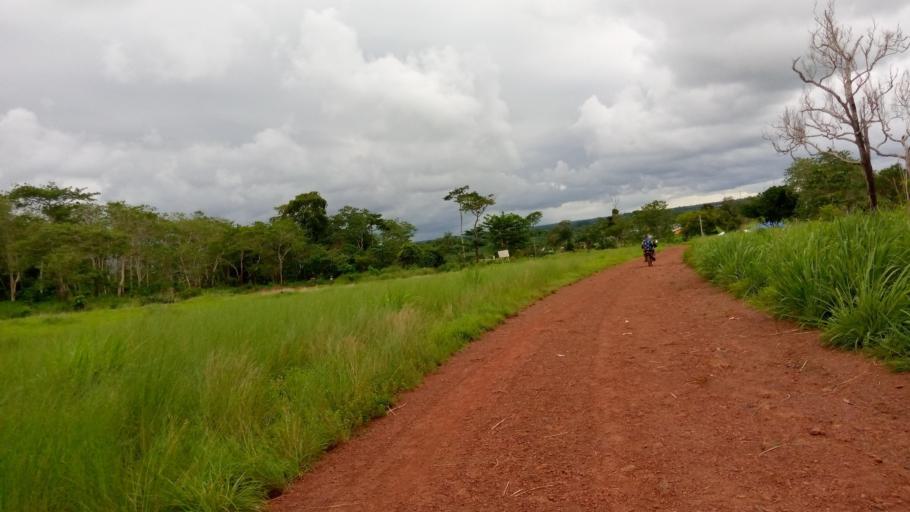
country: SL
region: Southern Province
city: Moyamba
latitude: 8.1620
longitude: -12.4521
